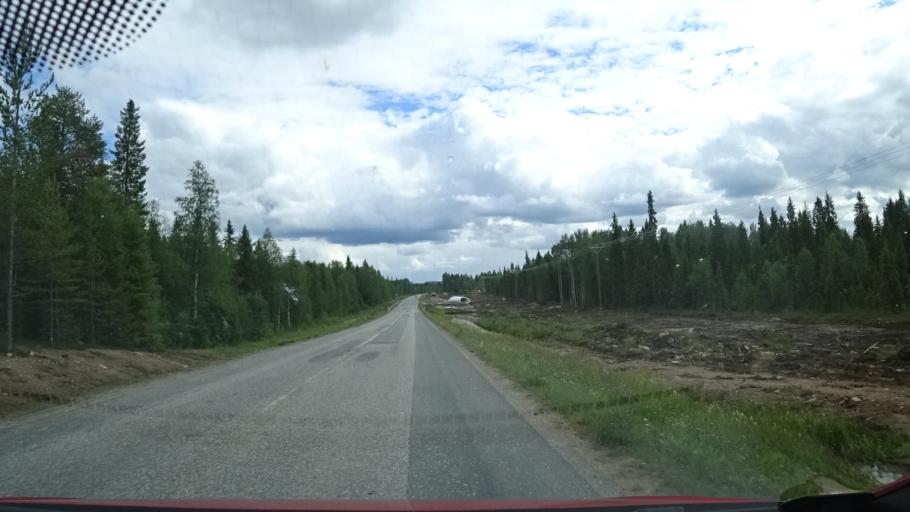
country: FI
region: Lapland
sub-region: Rovaniemi
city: Rovaniemi
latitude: 66.5399
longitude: 25.7190
